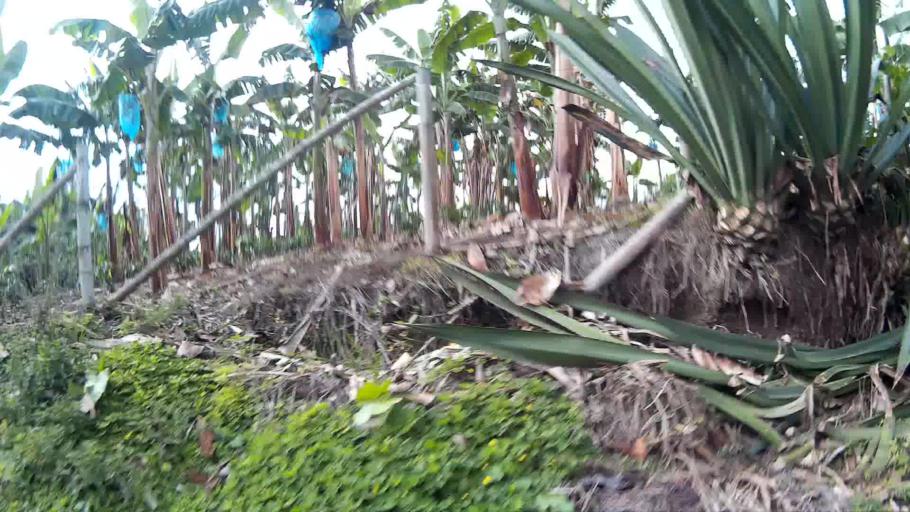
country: CO
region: Valle del Cauca
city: Ulloa
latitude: 4.7108
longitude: -75.6987
